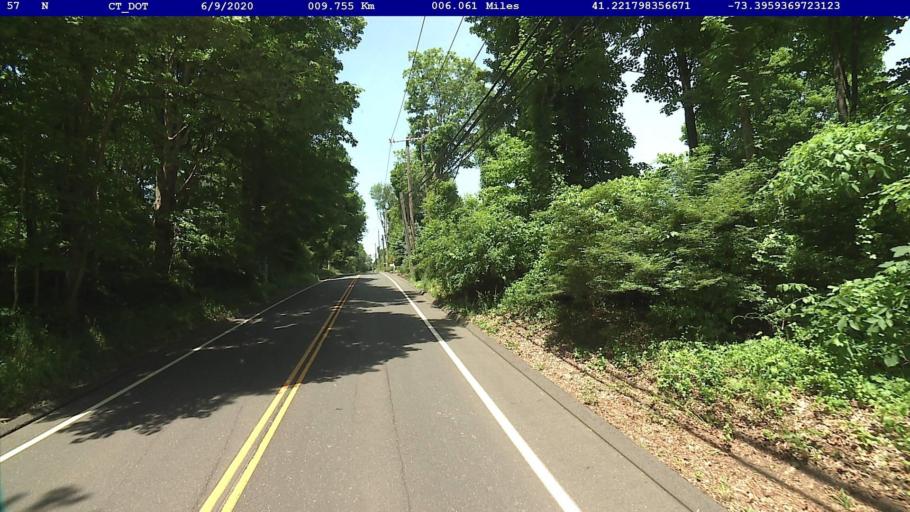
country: US
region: Connecticut
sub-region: Fairfield County
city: Wilton
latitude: 41.2218
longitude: -73.3960
